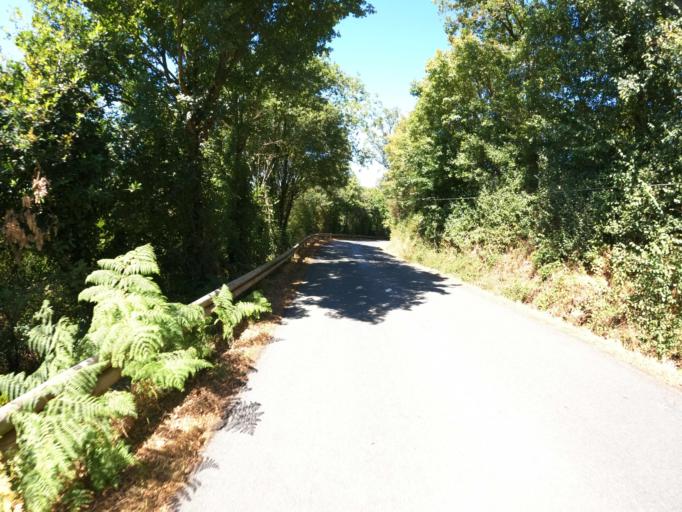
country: FR
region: Pays de la Loire
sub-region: Departement de la Vendee
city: Saint-Aubin-des-Ormeaux
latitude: 47.0021
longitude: -1.0245
